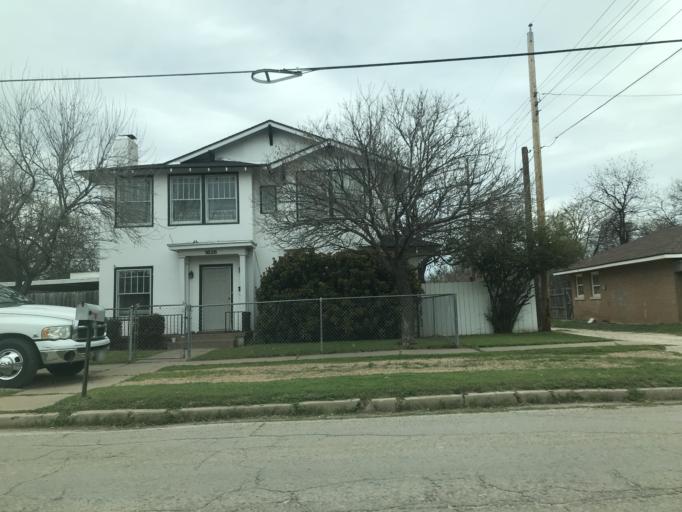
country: US
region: Texas
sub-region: Taylor County
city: Abilene
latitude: 32.4579
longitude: -99.7405
